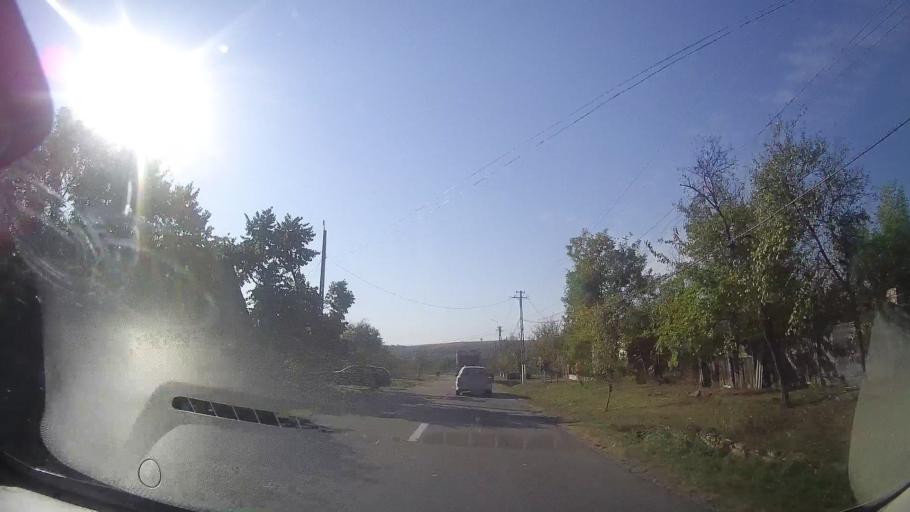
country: RO
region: Timis
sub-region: Oras Recas
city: Recas
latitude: 45.8522
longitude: 21.5162
